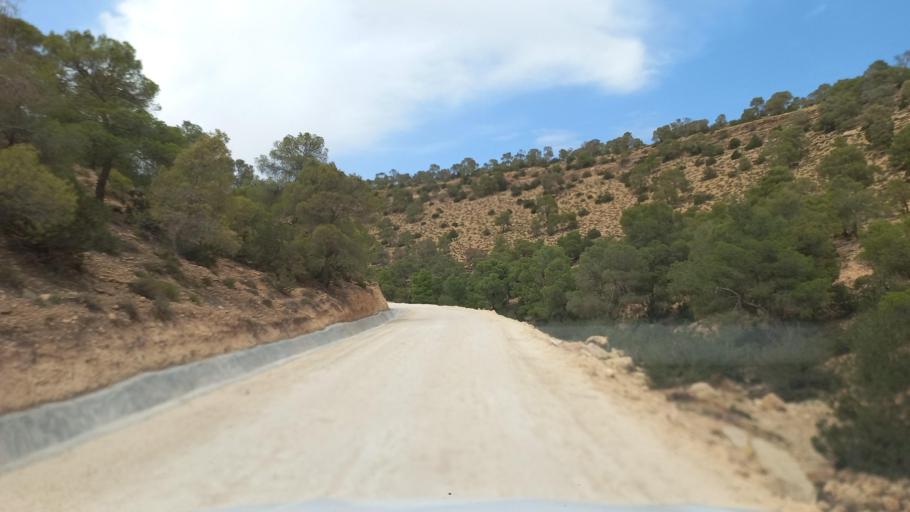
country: TN
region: Al Qasrayn
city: Kasserine
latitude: 35.3759
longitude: 8.8871
